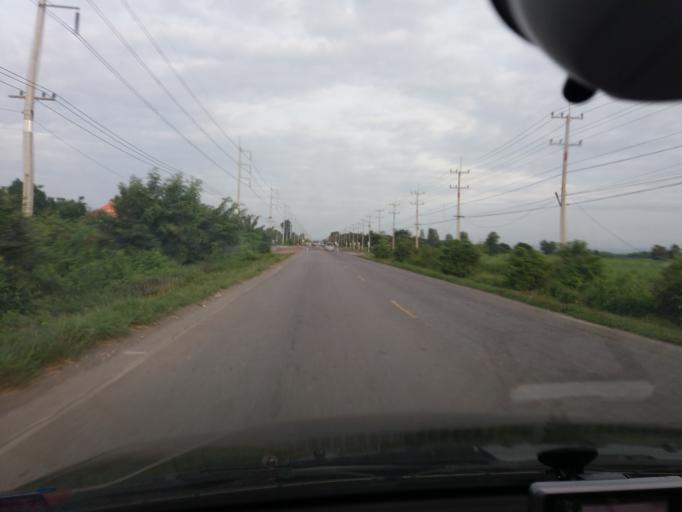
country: TH
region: Suphan Buri
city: U Thong
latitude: 14.3353
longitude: 99.7931
